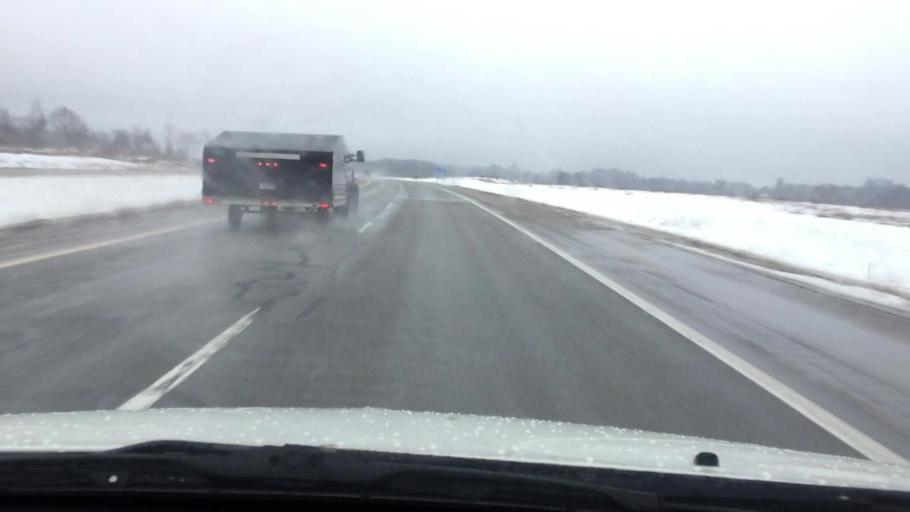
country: US
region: Michigan
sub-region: Wexford County
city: Cadillac
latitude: 44.2618
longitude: -85.3850
